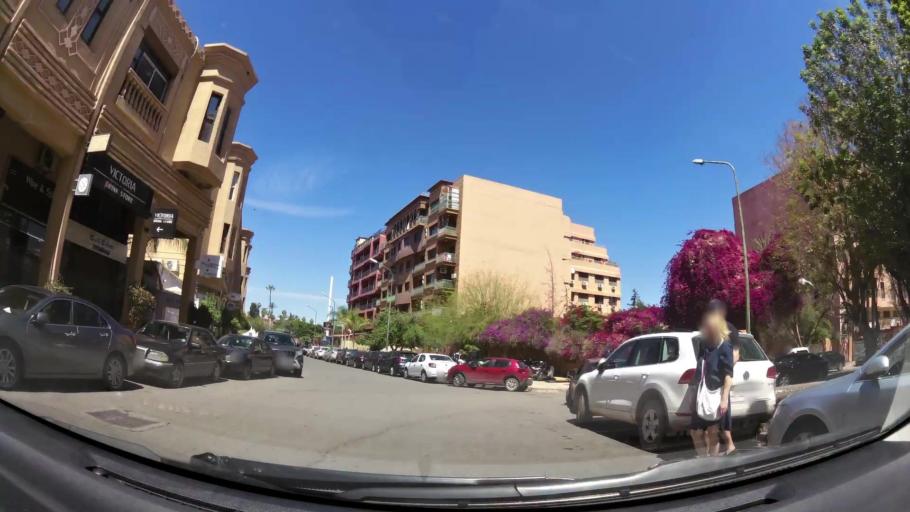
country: MA
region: Marrakech-Tensift-Al Haouz
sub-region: Marrakech
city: Marrakesh
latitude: 31.6286
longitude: -8.0075
